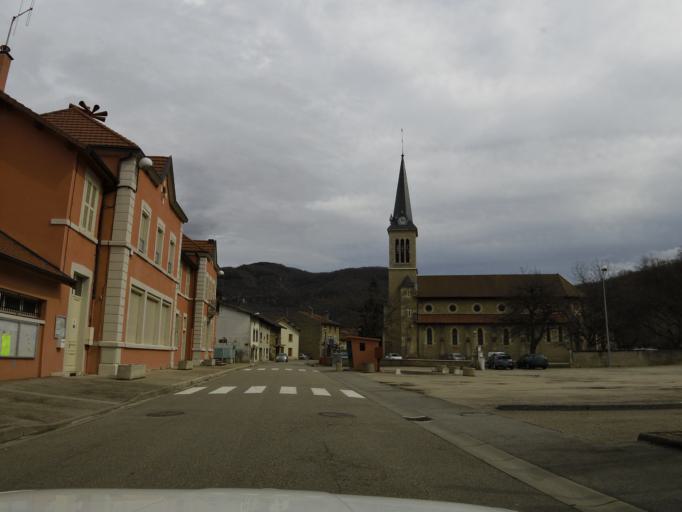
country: FR
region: Rhone-Alpes
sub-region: Departement de l'Ain
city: Vaux-en-Bugey
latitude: 45.9433
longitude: 5.3620
